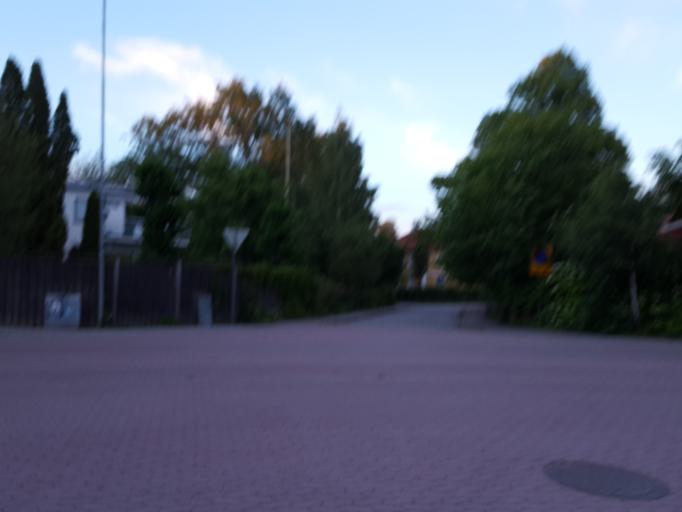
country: SE
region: Uppsala
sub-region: Uppsala Kommun
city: Uppsala
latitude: 59.8477
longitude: 17.6221
